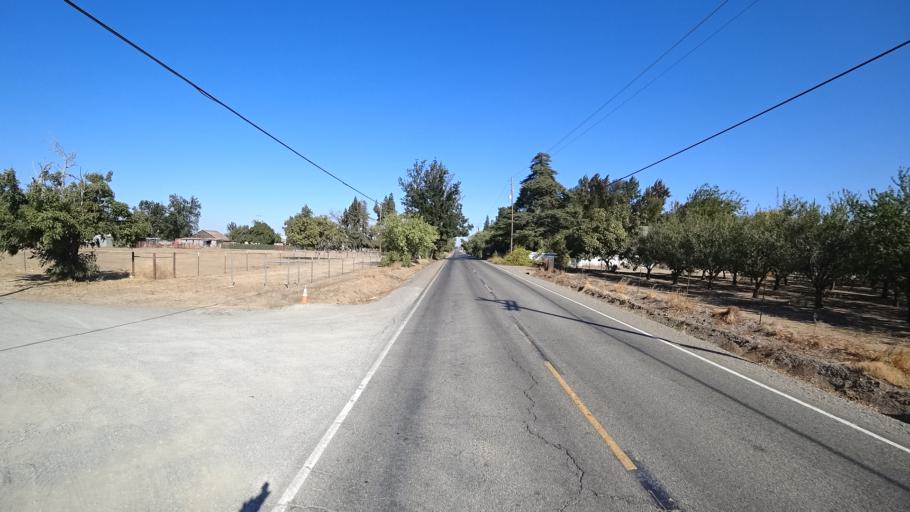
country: US
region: California
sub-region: Yolo County
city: Cottonwood
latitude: 38.6567
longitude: -121.9711
